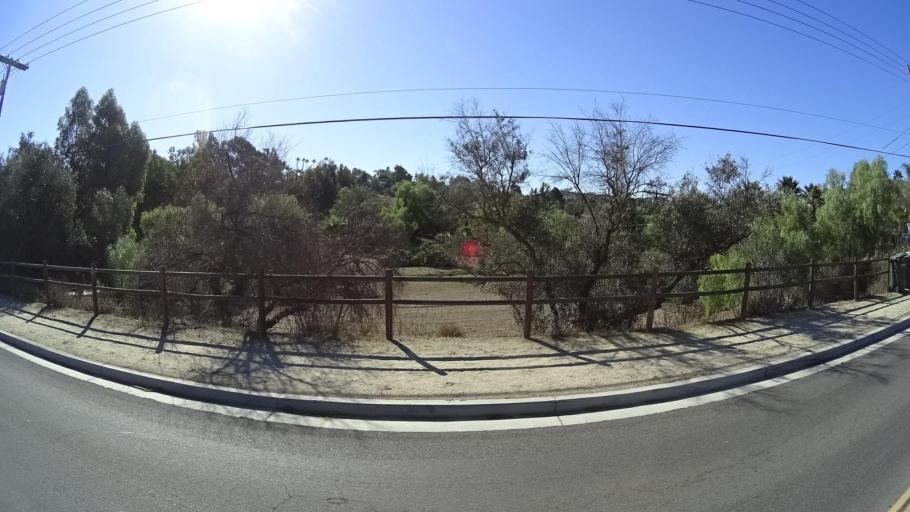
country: US
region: California
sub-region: San Diego County
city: Bonita
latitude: 32.6763
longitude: -117.0098
